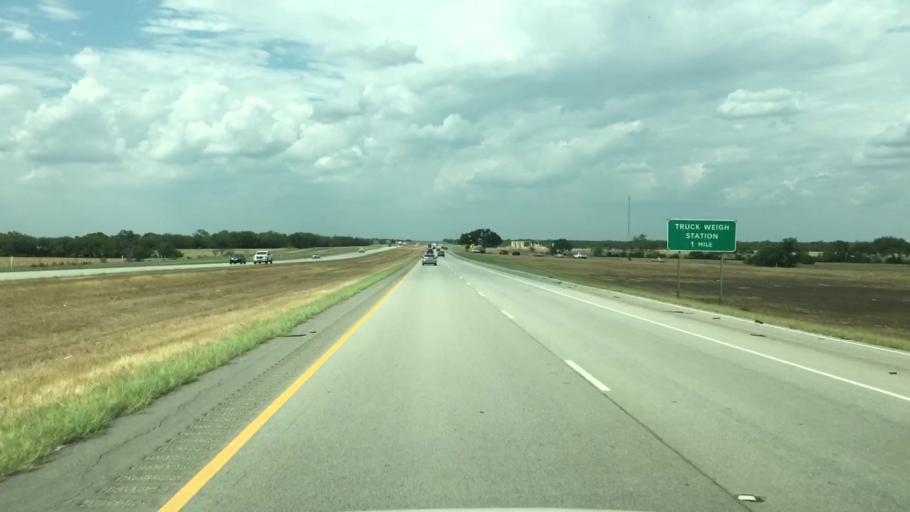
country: US
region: Texas
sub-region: Live Oak County
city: Three Rivers
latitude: 28.5299
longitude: -98.1875
